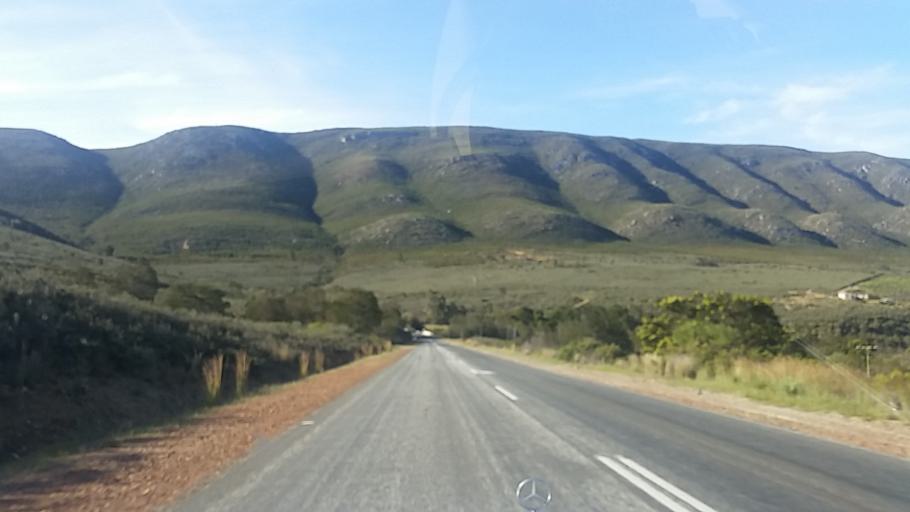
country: ZA
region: Western Cape
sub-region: Eden District Municipality
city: Knysna
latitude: -33.7657
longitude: 22.9622
